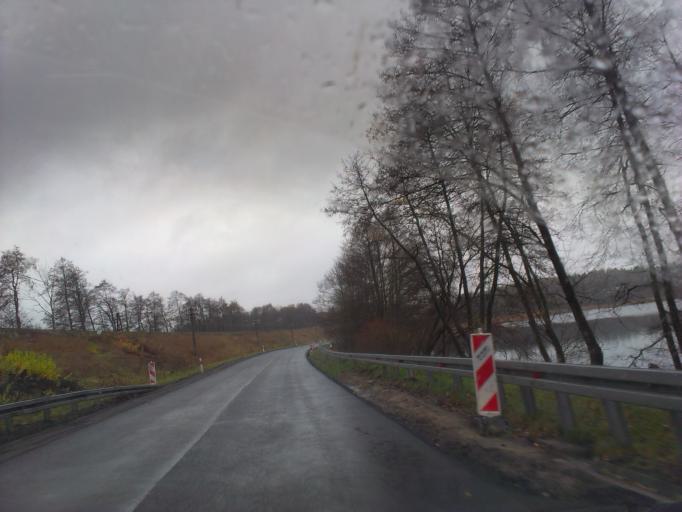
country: PL
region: West Pomeranian Voivodeship
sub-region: Powiat szczecinecki
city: Lubowo
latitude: 53.6171
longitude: 16.4483
